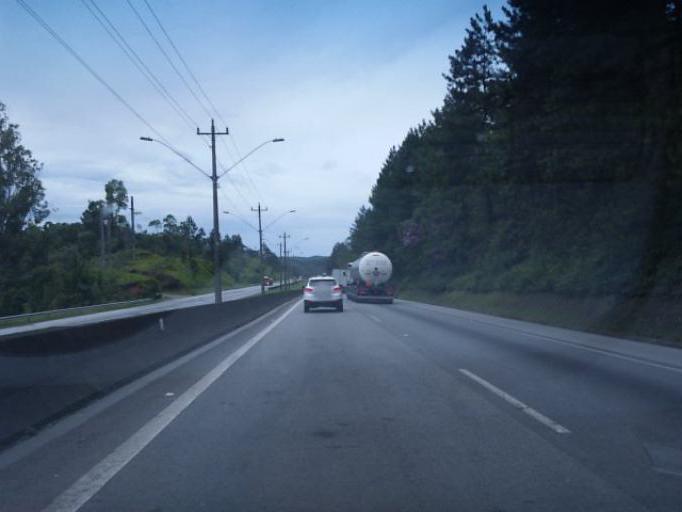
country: BR
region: Sao Paulo
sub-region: Sao Lourenco Da Serra
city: Sao Lourenco da Serra
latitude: -23.8682
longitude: -46.9550
